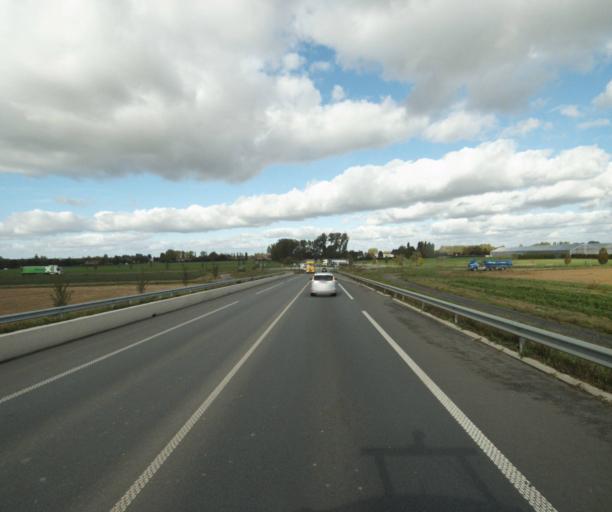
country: FR
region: Nord-Pas-de-Calais
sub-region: Departement du Nord
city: Houplines
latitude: 50.6769
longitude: 2.9181
